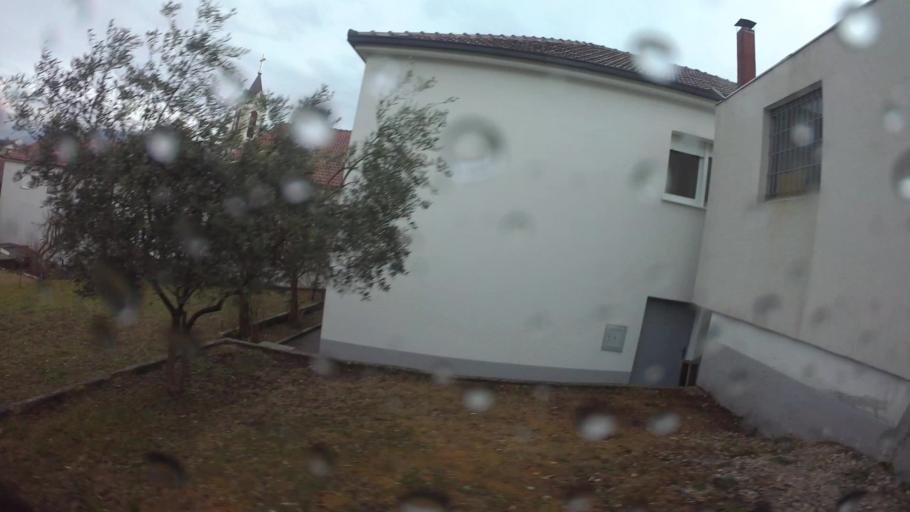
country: BA
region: Federation of Bosnia and Herzegovina
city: Cim
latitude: 43.3499
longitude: 17.7773
